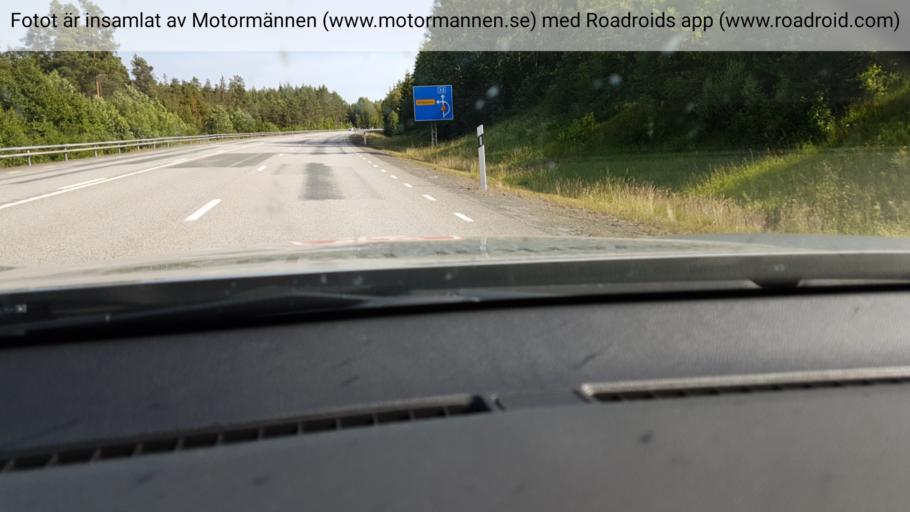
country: SE
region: Joenkoeping
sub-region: Aneby Kommun
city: Aneby
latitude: 57.7849
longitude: 14.8814
